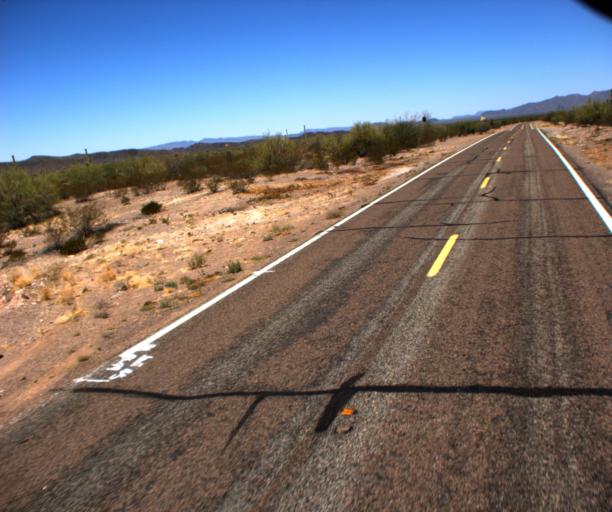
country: US
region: Arizona
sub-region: Pima County
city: Ajo
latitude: 32.2266
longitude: -112.7062
